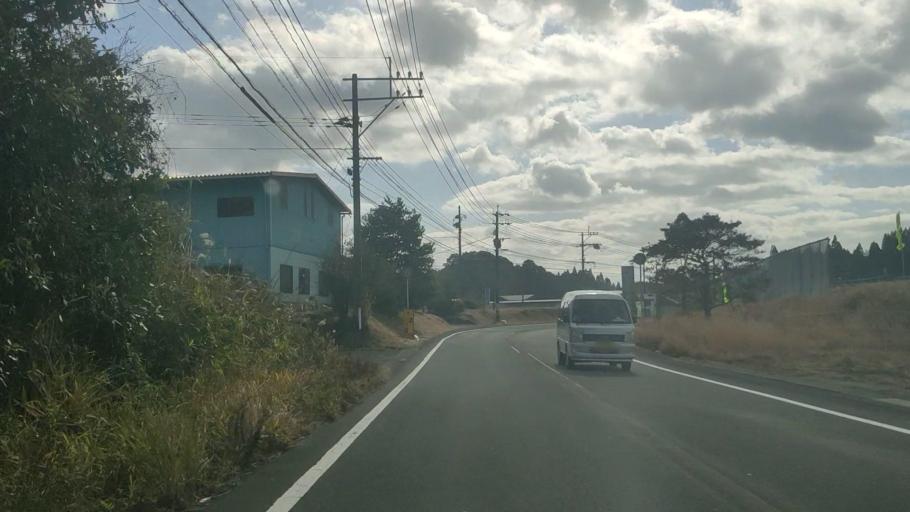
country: JP
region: Kagoshima
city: Okuchi-shinohara
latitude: 31.9257
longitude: 130.7012
